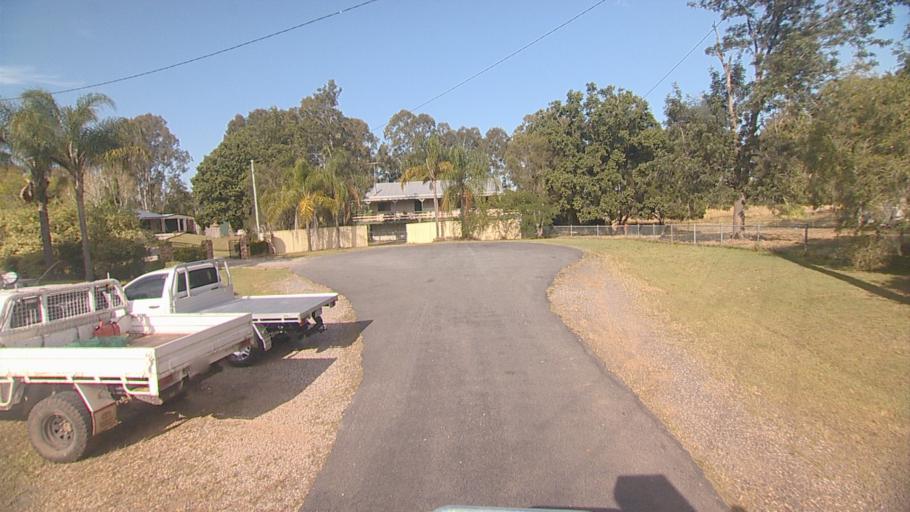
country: AU
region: Queensland
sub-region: Logan
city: Chambers Flat
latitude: -27.7505
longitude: 153.0599
